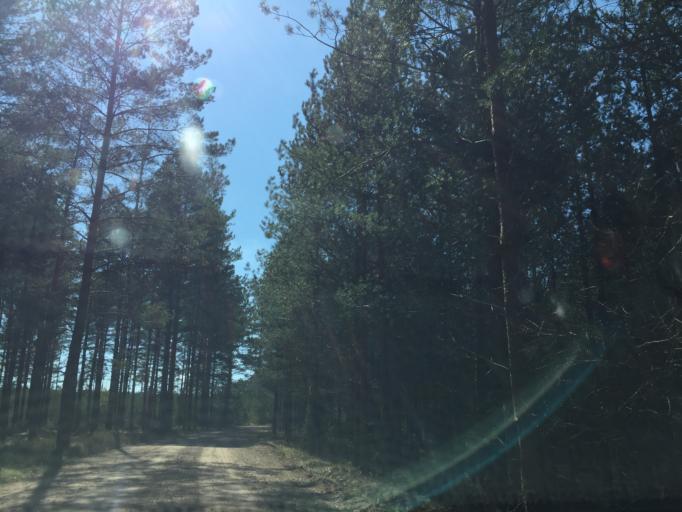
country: LV
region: Strenci
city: Strenci
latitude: 57.5963
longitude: 25.7039
